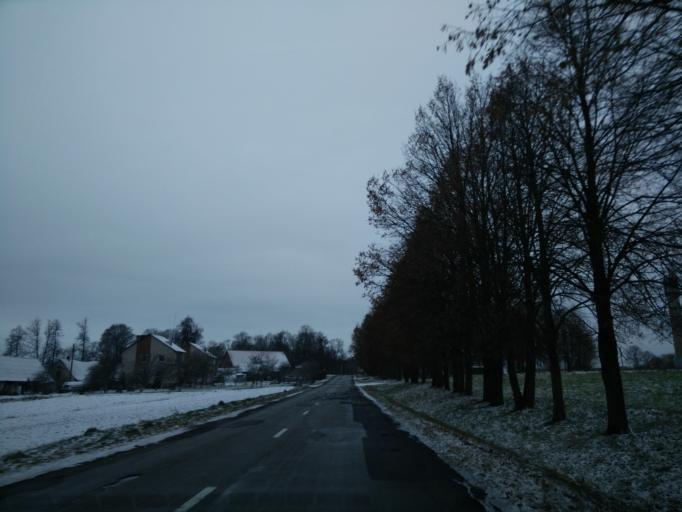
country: LT
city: Tytuveneliai
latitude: 55.4874
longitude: 23.3309
